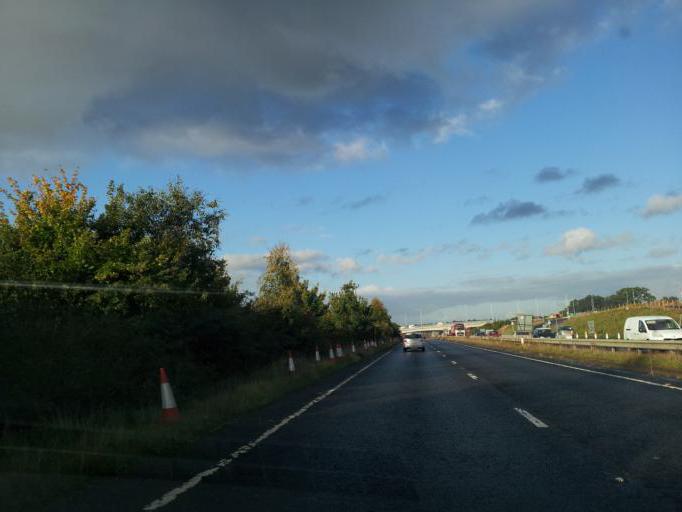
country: GB
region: England
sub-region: Norfolk
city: Surlingham
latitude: 52.6258
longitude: 1.3890
